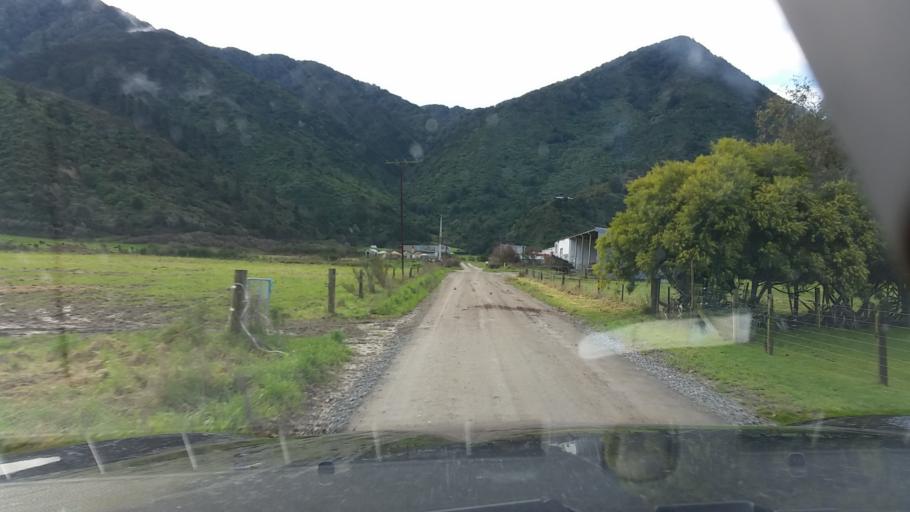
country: NZ
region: Marlborough
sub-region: Marlborough District
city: Picton
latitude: -41.3163
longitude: 173.9683
